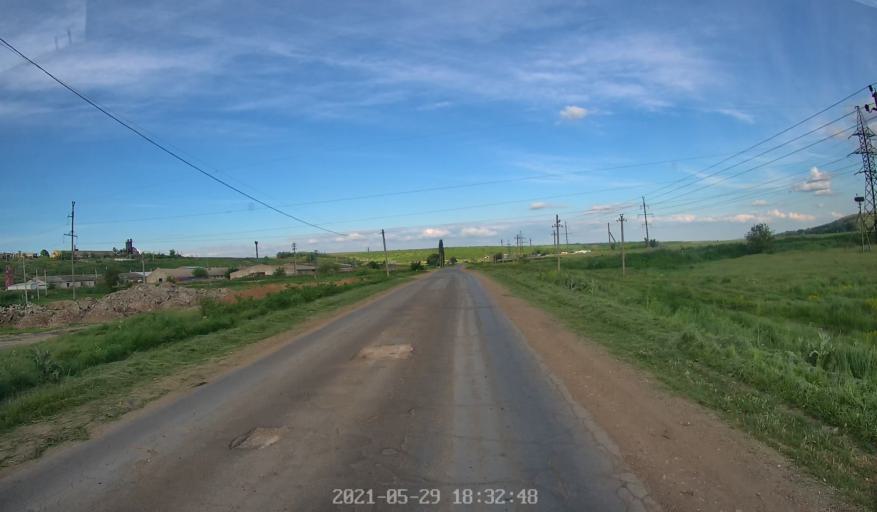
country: MD
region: Chisinau
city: Singera
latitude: 46.8173
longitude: 28.8964
